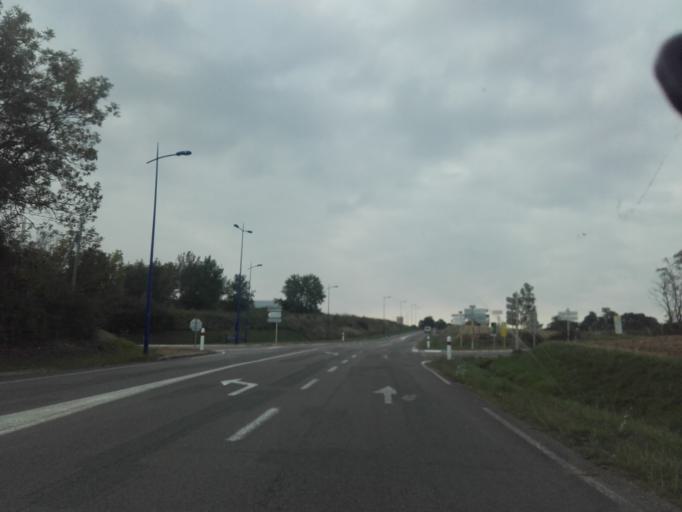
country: FR
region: Bourgogne
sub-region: Departement de Saone-et-Loire
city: Charnay-les-Macon
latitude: 46.2843
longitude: 4.7758
